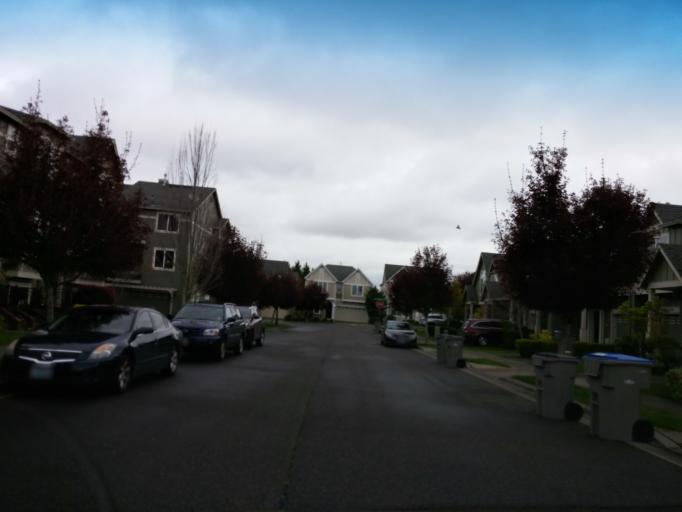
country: US
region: Oregon
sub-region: Washington County
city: Oak Hills
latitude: 45.5369
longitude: -122.8498
